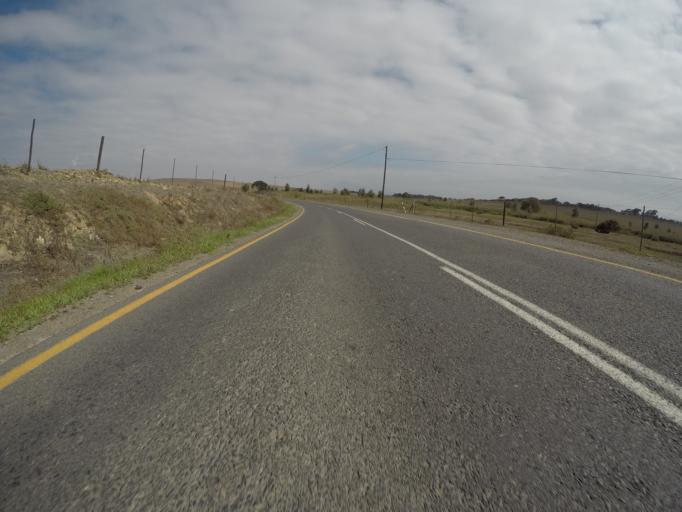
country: ZA
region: Western Cape
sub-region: City of Cape Town
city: Sunset Beach
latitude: -33.7830
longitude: 18.5560
